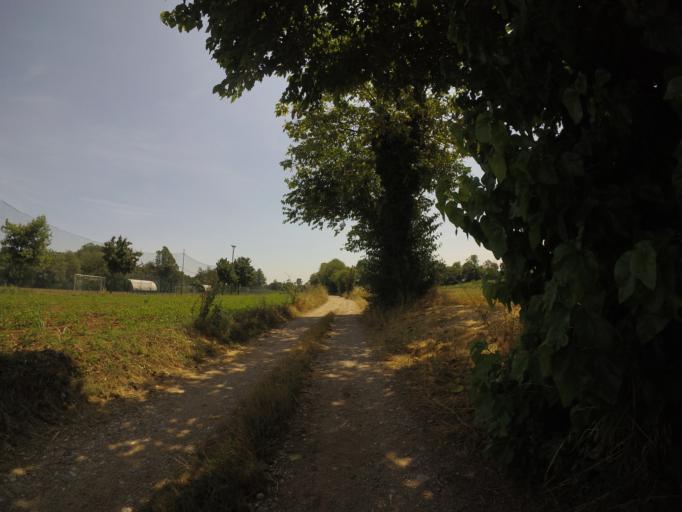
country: IT
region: Friuli Venezia Giulia
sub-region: Provincia di Udine
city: Basiliano
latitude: 45.9797
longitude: 13.0908
